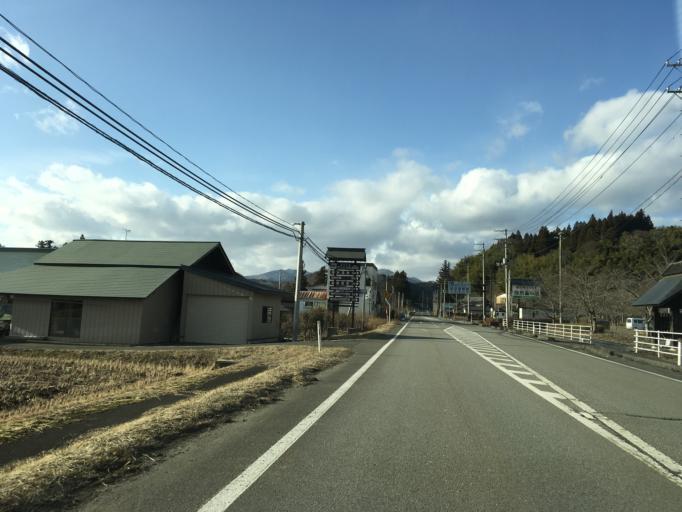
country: JP
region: Miyagi
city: Furukawa
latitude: 38.7936
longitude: 140.8451
